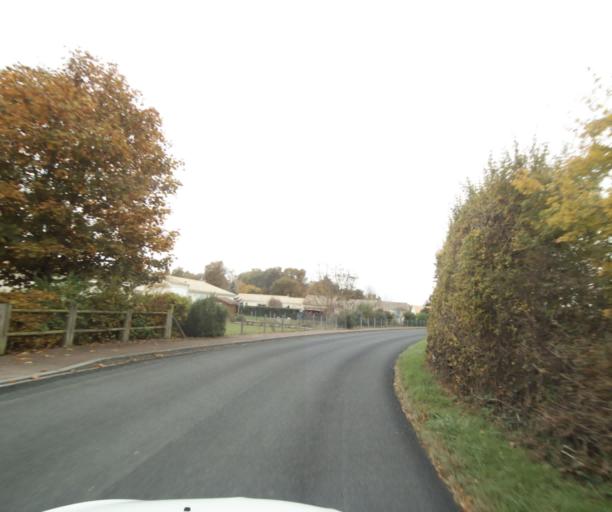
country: FR
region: Poitou-Charentes
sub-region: Departement de la Charente-Maritime
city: Les Gonds
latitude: 45.7341
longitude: -0.6200
